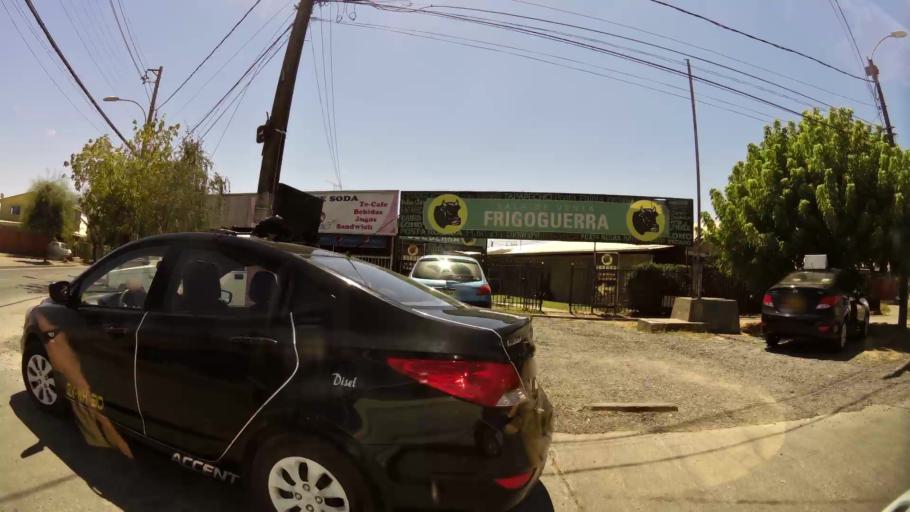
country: CL
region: Maule
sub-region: Provincia de Curico
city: Curico
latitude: -34.9818
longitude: -71.2174
